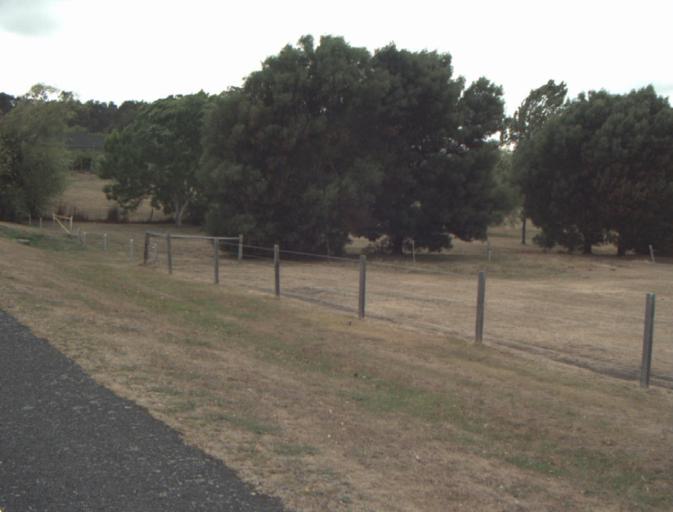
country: AU
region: Tasmania
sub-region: Launceston
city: Mayfield
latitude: -41.3306
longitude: 147.0569
